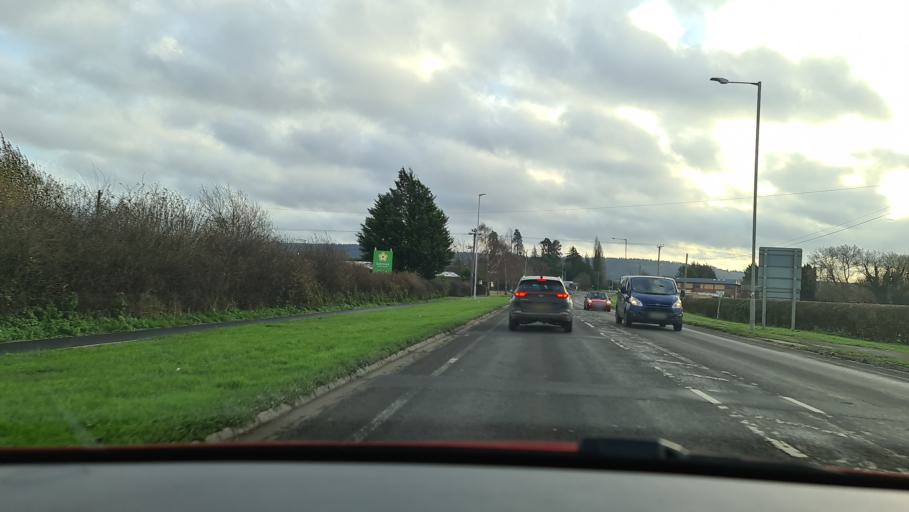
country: GB
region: England
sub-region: Buckinghamshire
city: Weston Turville
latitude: 51.7766
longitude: -0.7603
